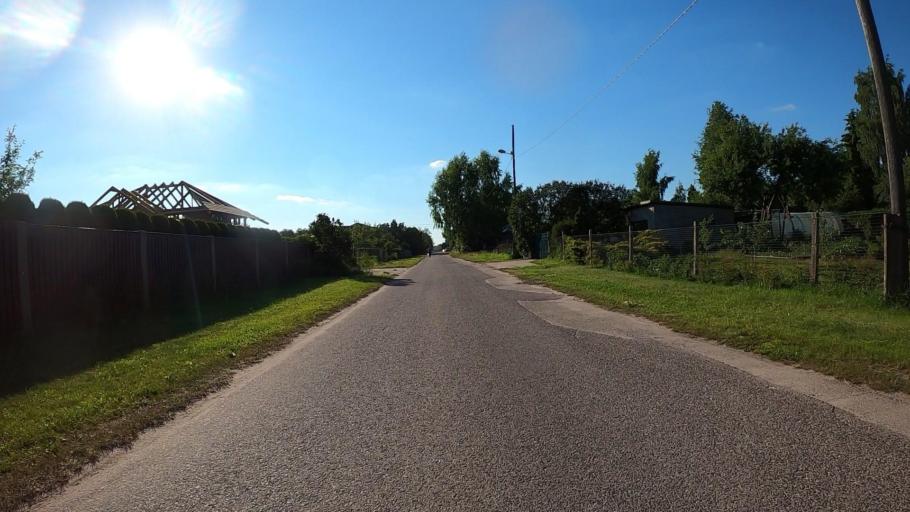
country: LV
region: Stopini
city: Ulbroka
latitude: 56.9050
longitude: 24.2252
